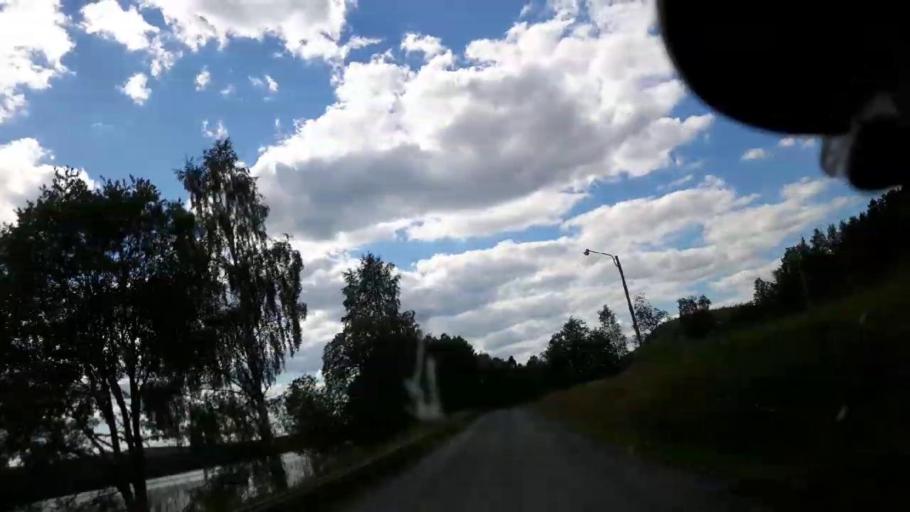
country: SE
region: Jaemtland
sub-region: Braecke Kommun
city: Braecke
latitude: 62.7171
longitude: 15.5970
